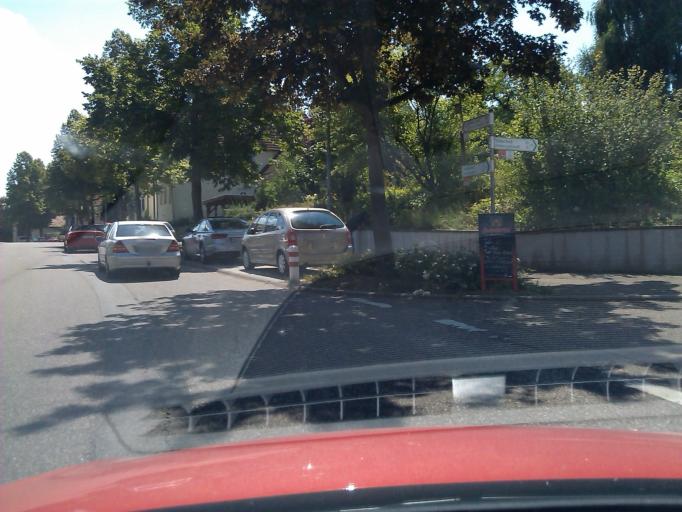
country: DE
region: Baden-Wuerttemberg
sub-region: Regierungsbezirk Stuttgart
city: Brackenheim
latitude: 49.1039
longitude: 9.0483
